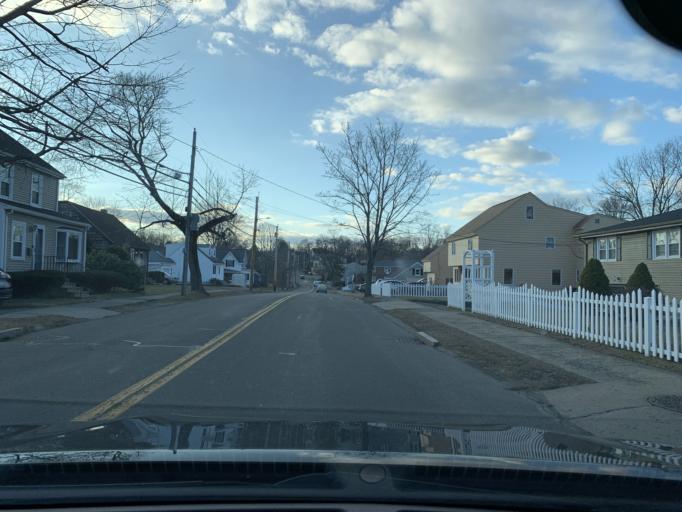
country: US
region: Massachusetts
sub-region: Essex County
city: Danvers
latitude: 42.5653
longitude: -70.9453
